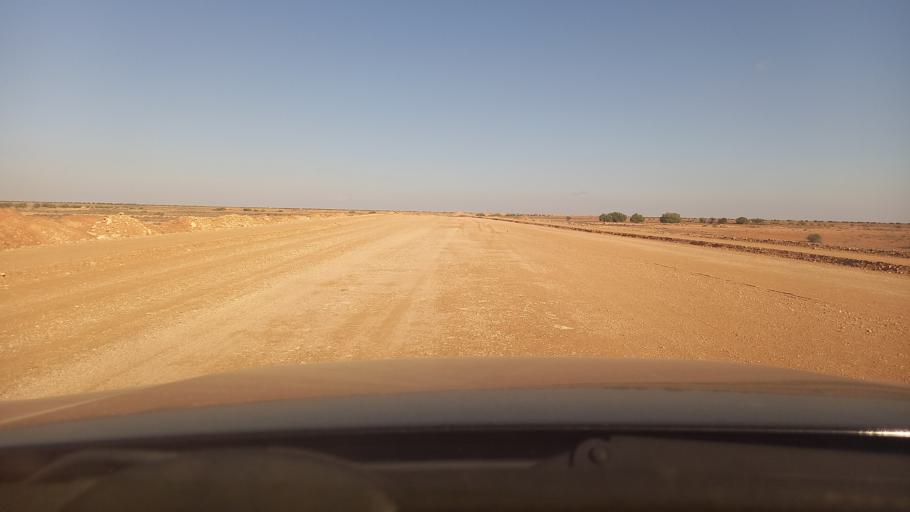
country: TN
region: Madanin
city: Medenine
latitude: 33.1396
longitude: 10.5054
